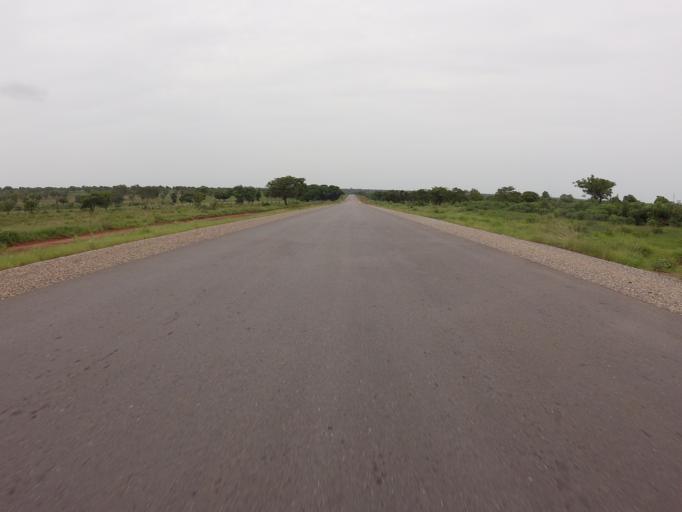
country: GH
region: Northern
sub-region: Yendi
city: Yendi
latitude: 9.2667
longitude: 0.0182
